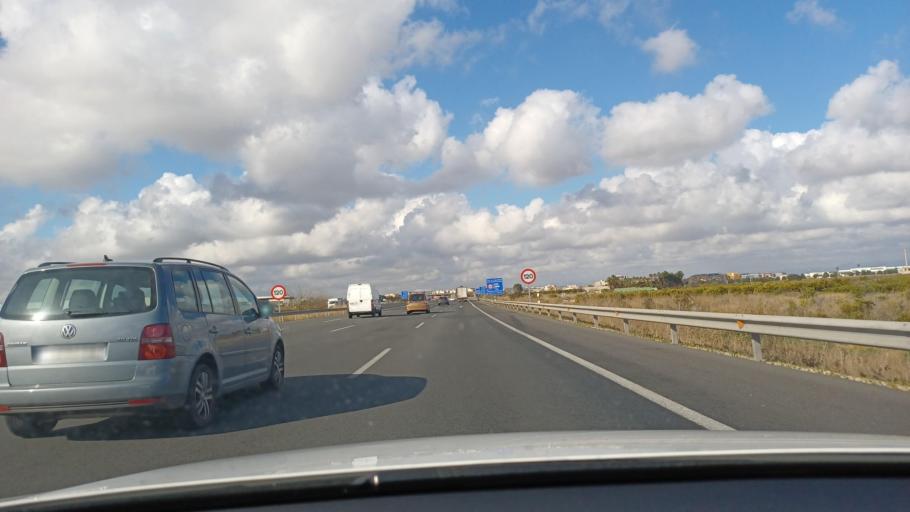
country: ES
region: Valencia
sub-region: Provincia de Valencia
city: Alcasser
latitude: 39.3543
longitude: -0.4363
